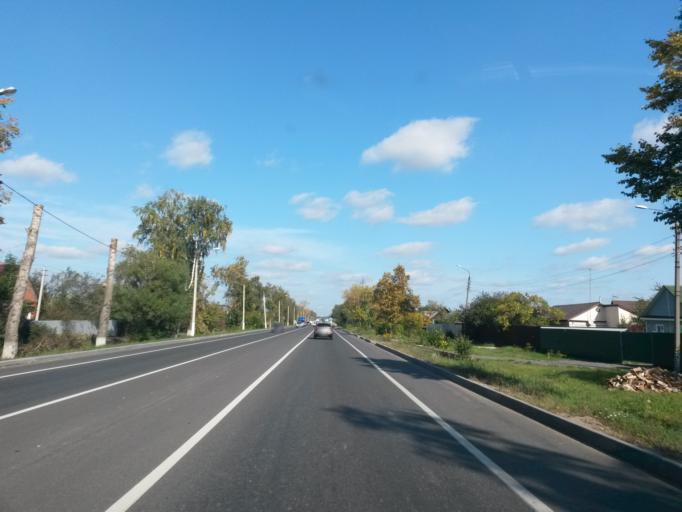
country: RU
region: Moskovskaya
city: L'vovskiy
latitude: 55.3250
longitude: 37.5286
